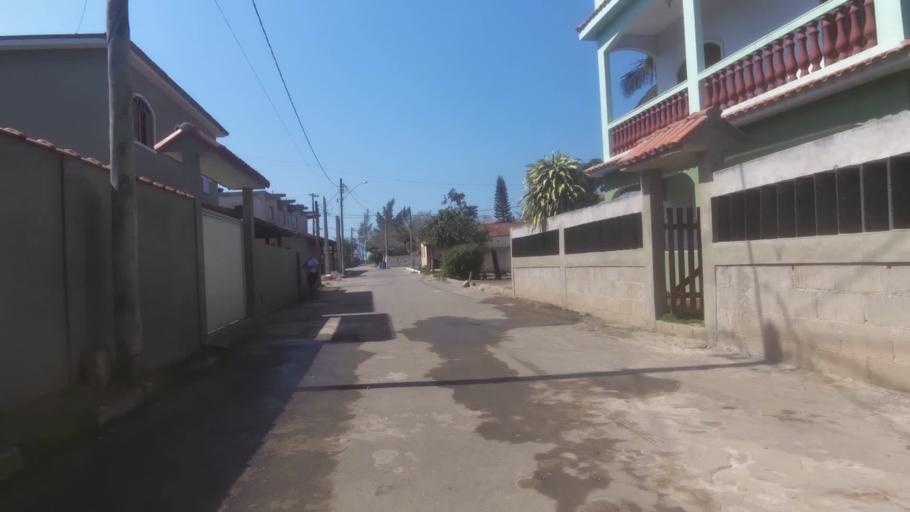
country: BR
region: Espirito Santo
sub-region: Marataizes
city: Marataizes
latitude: -21.0905
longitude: -40.8453
